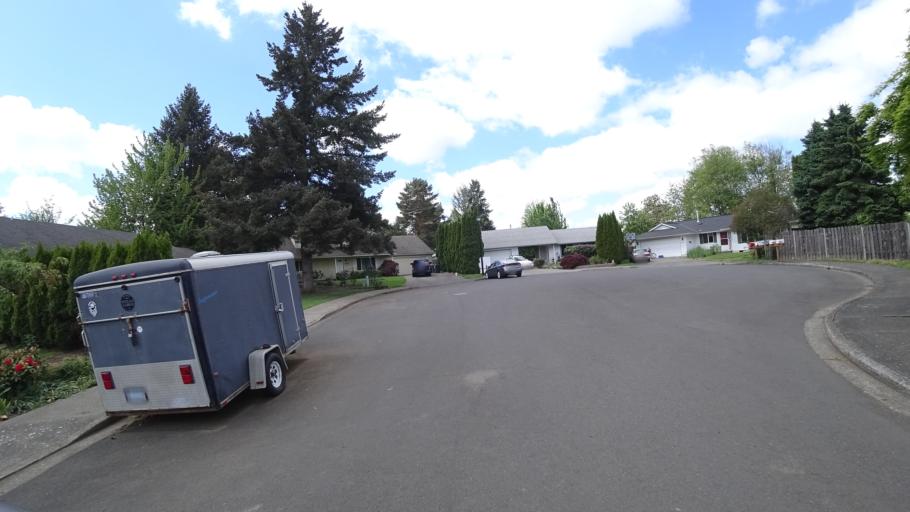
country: US
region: Oregon
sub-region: Washington County
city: Aloha
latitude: 45.5025
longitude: -122.8933
